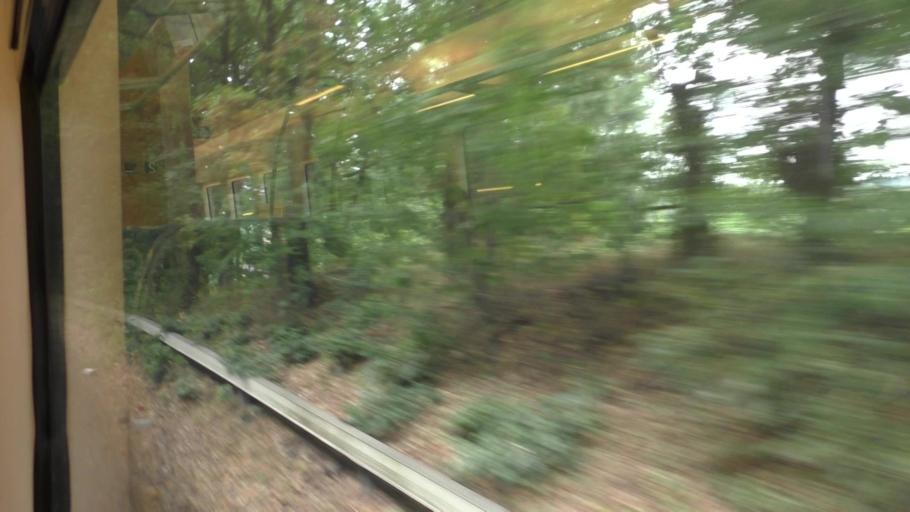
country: DE
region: Saxony
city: Goerlitz
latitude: 51.1236
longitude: 14.9679
